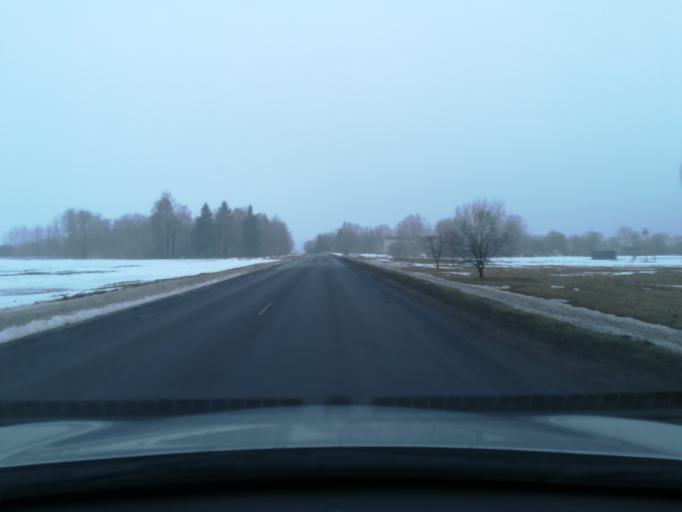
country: EE
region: Harju
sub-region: Raasiku vald
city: Arukula
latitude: 59.3458
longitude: 25.1039
